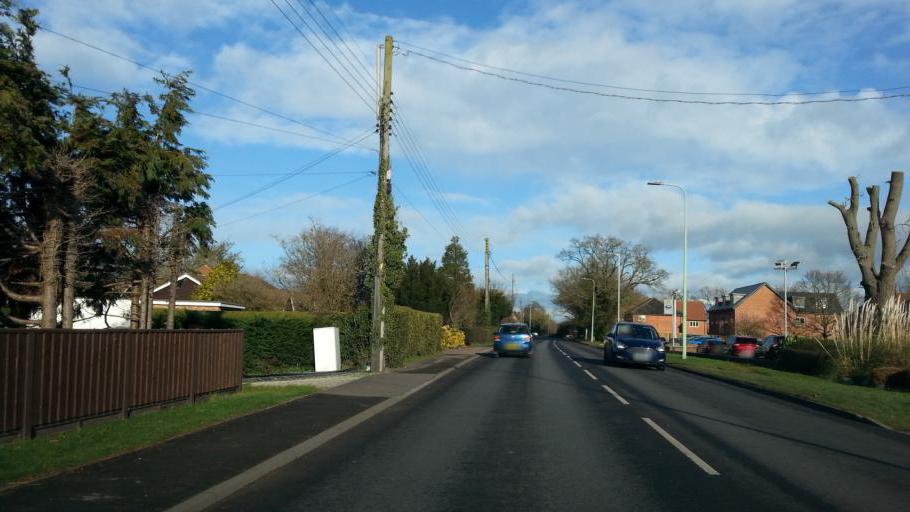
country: GB
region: England
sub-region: Suffolk
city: Halesworth
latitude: 52.3518
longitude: 1.5095
